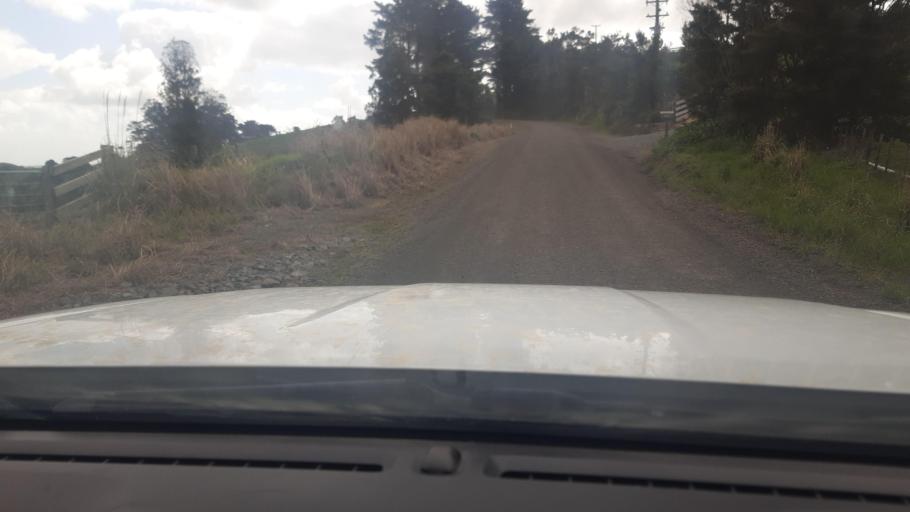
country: NZ
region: Northland
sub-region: Far North District
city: Kaitaia
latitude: -35.0650
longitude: 173.3272
